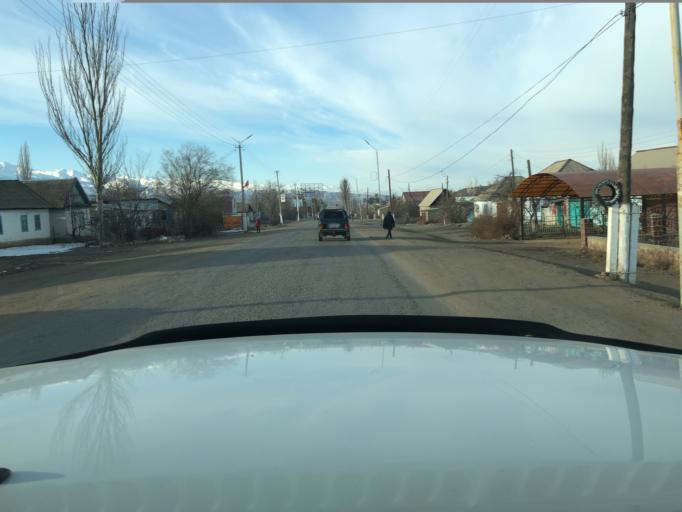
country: KG
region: Ysyk-Koel
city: Pokrovka
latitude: 42.3454
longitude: 78.0122
